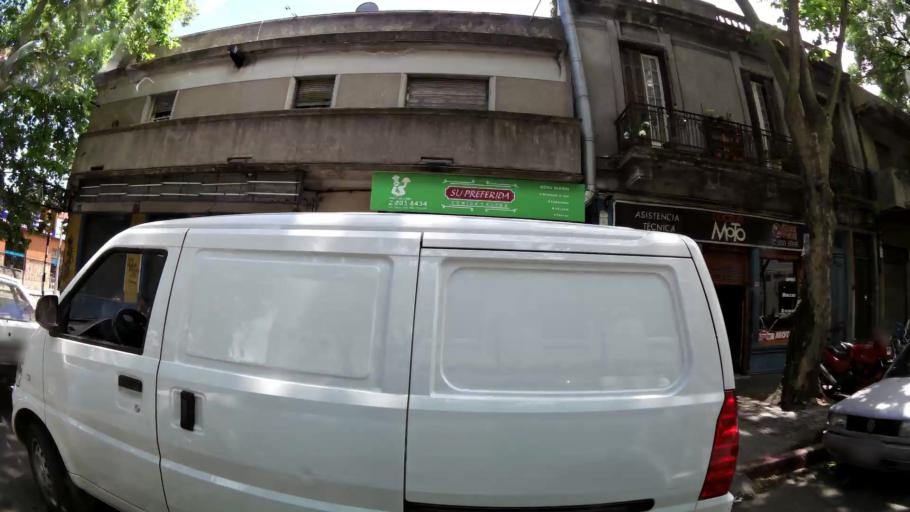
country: UY
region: Montevideo
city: Montevideo
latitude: -34.8741
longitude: -56.1841
